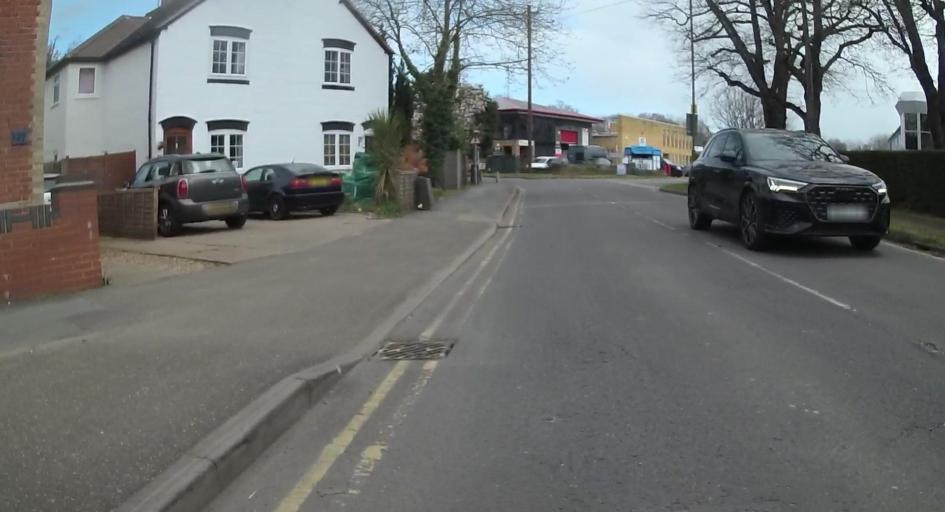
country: GB
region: England
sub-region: Surrey
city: West Byfleet
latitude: 51.3429
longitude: -0.4992
